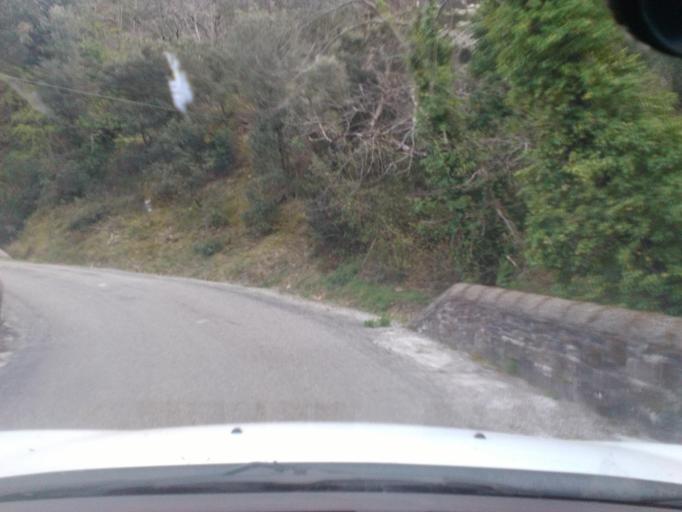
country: FR
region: Languedoc-Roussillon
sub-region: Departement du Gard
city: Lasalle
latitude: 44.0948
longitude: 3.8015
